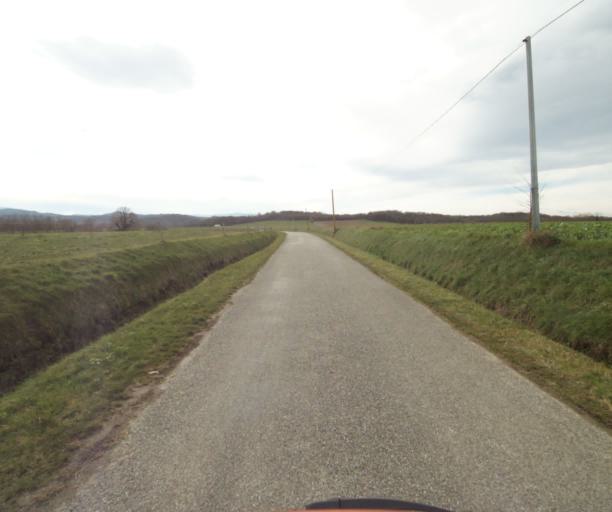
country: FR
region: Midi-Pyrenees
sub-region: Departement de l'Ariege
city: La Tour-du-Crieu
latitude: 43.0848
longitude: 1.7134
